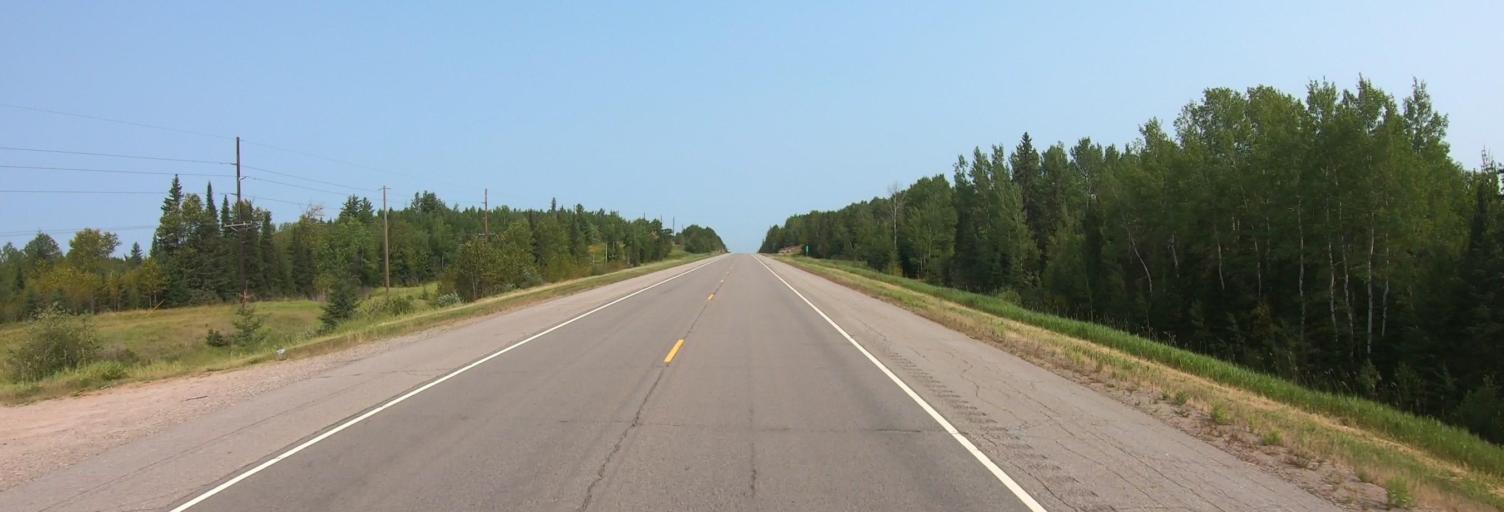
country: US
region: Minnesota
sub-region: Saint Louis County
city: Mountain Iron
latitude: 47.9967
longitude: -92.8309
